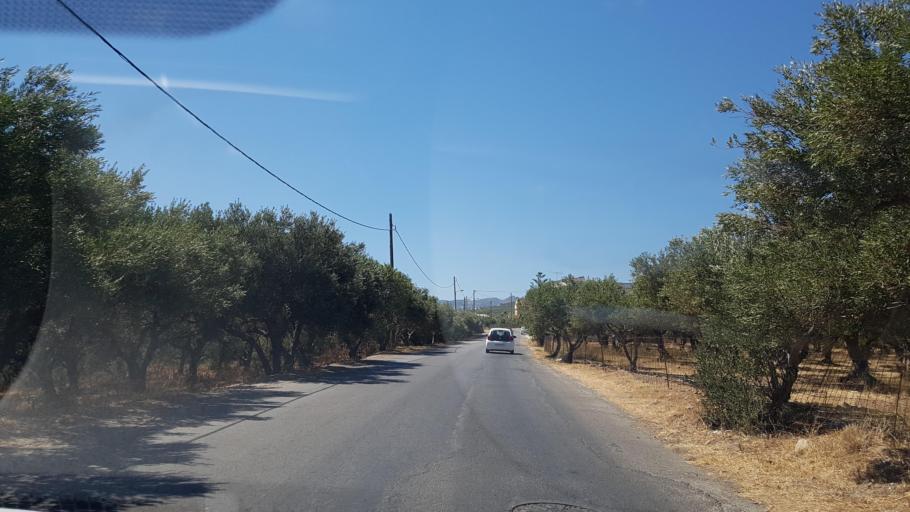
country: GR
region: Crete
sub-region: Nomos Chanias
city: Kissamos
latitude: 35.4939
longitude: 23.6850
